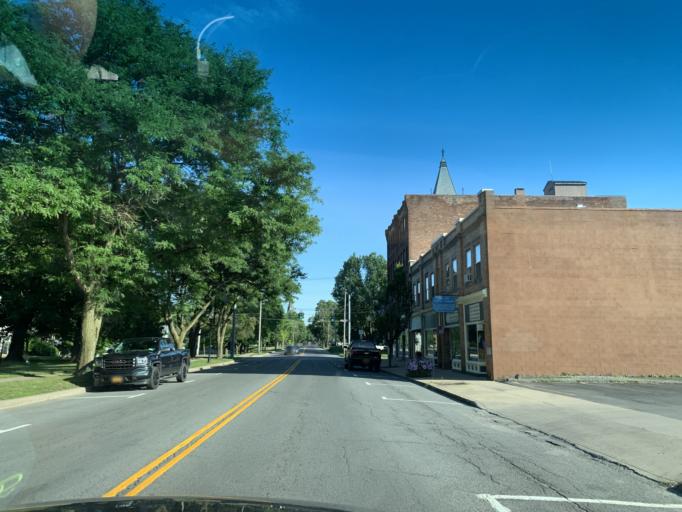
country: US
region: New York
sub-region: Madison County
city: Oneida
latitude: 43.0935
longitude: -75.6511
